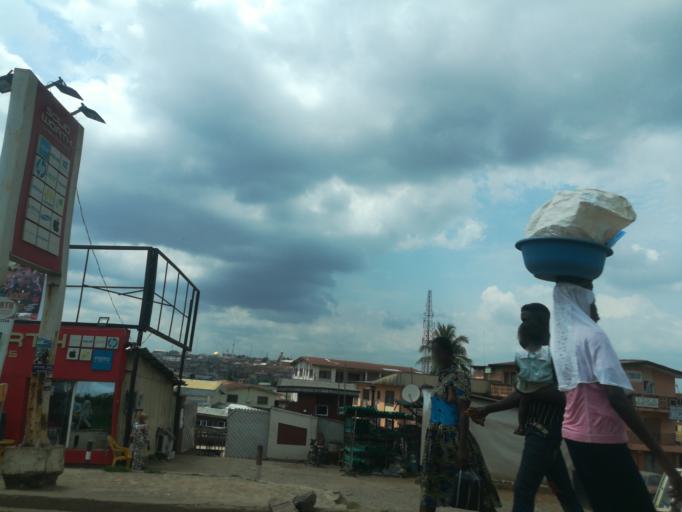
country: NG
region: Oyo
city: Ibadan
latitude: 7.4057
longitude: 3.9436
